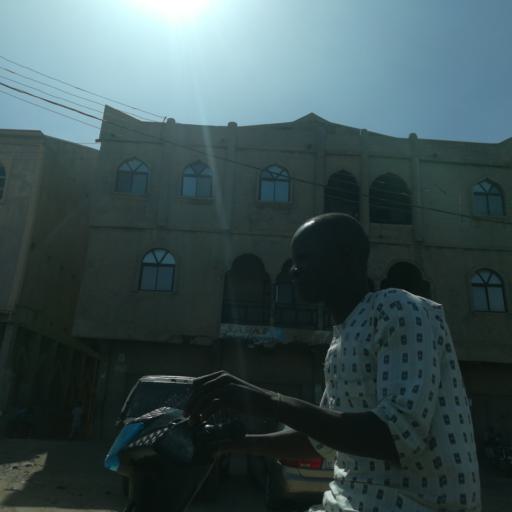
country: NG
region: Kano
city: Kano
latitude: 12.0003
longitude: 8.5272
